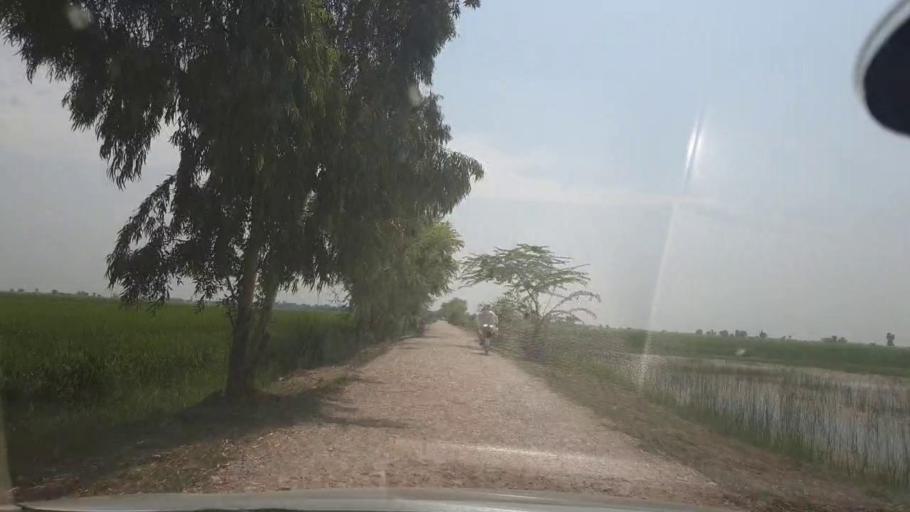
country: PK
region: Sindh
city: Thul
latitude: 28.1663
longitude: 68.6495
